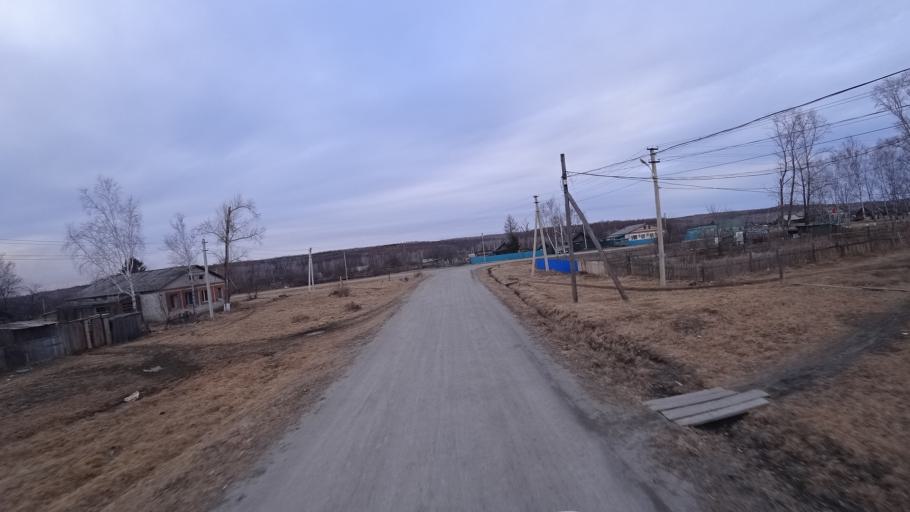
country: RU
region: Amur
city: Bureya
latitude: 50.0194
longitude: 129.7686
